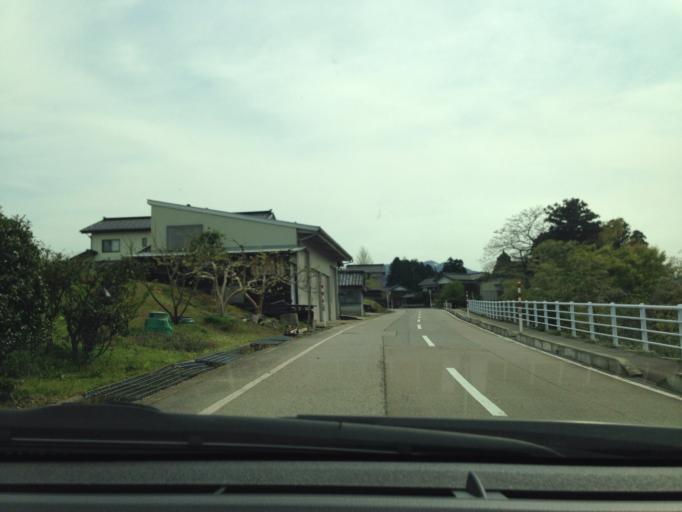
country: JP
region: Toyama
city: Fukumitsu
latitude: 36.5243
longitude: 136.8601
